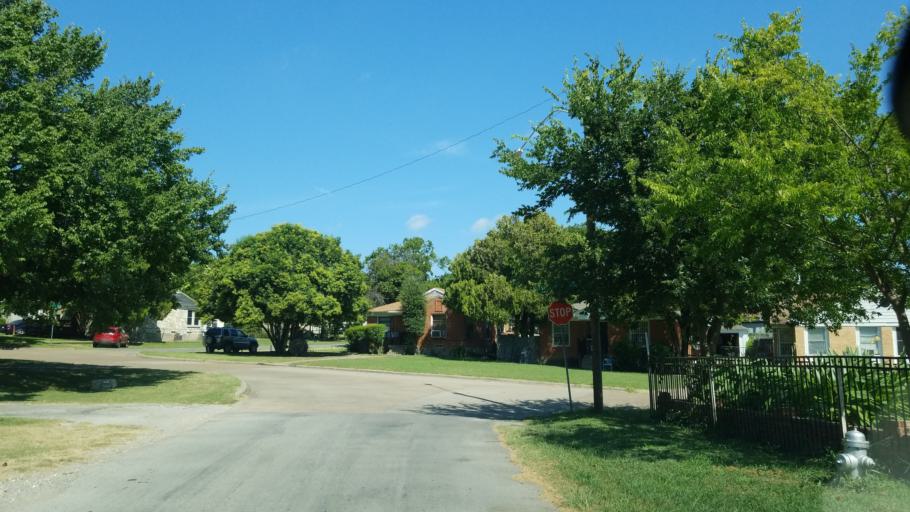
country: US
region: Texas
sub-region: Dallas County
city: Dallas
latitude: 32.7314
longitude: -96.7956
